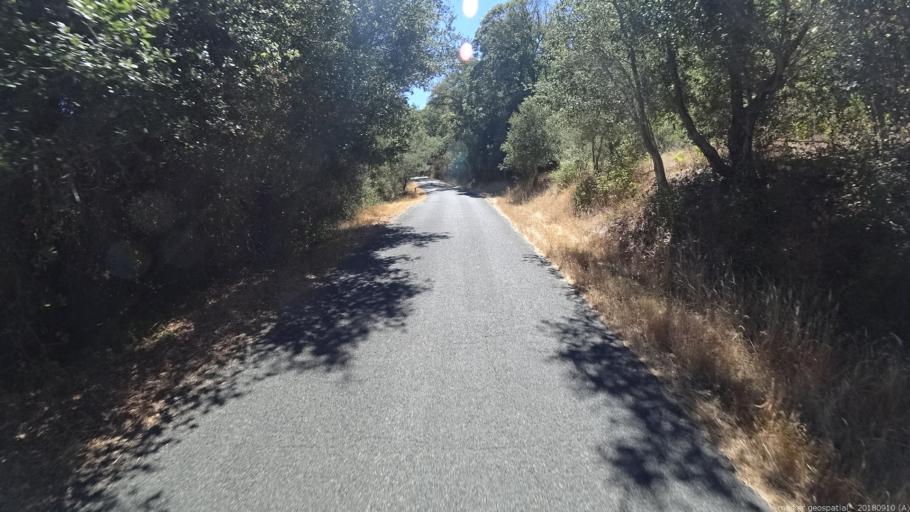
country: US
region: California
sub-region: Monterey County
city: Carmel Valley Village
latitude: 36.4335
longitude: -121.7917
